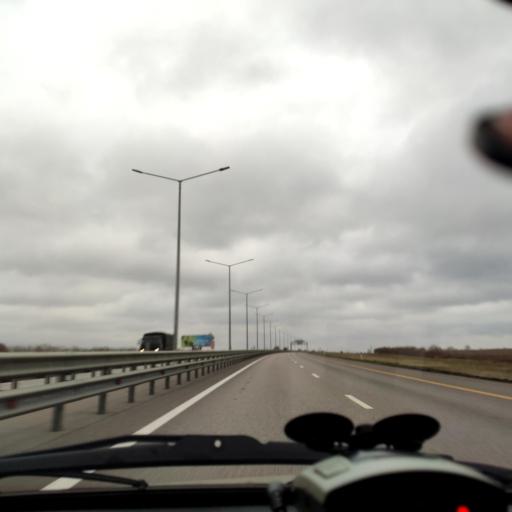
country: RU
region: Voronezj
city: Novaya Usman'
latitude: 51.6025
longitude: 39.3396
